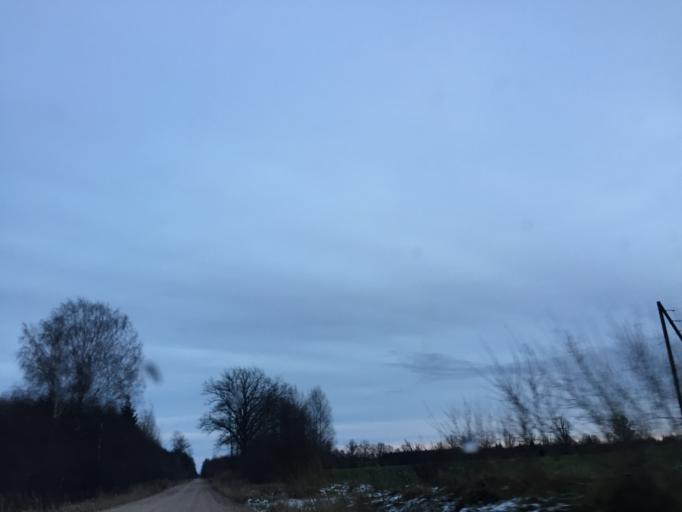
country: LV
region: Burtnieki
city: Matisi
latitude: 57.6330
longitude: 25.1163
